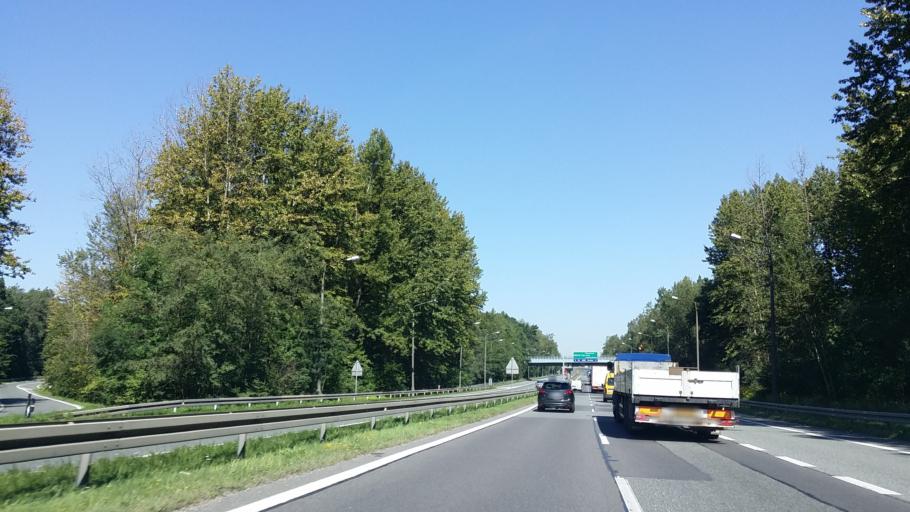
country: PL
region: Silesian Voivodeship
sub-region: Myslowice
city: Myslowice
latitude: 50.1800
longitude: 19.1682
